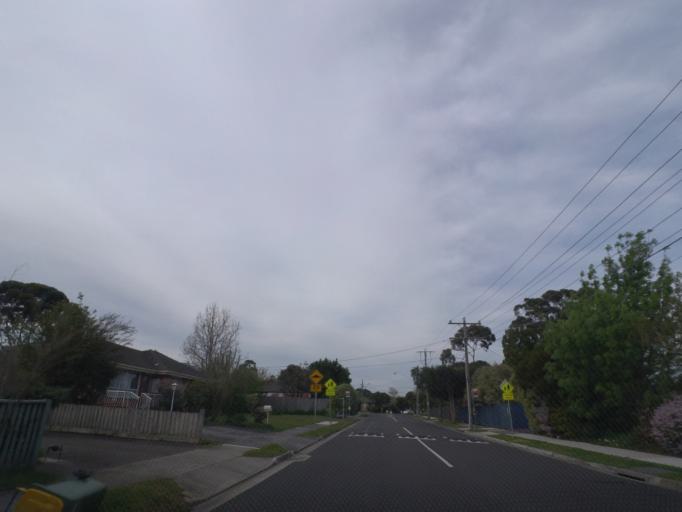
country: AU
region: Victoria
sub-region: Knox
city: Knoxfield
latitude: -37.8892
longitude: 145.2435
